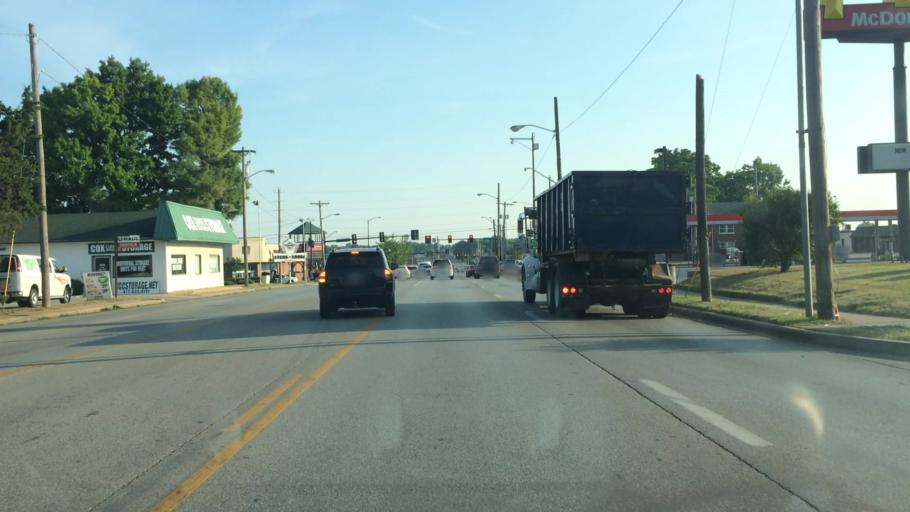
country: US
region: Missouri
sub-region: Greene County
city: Springfield
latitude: 37.2080
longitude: -93.2760
